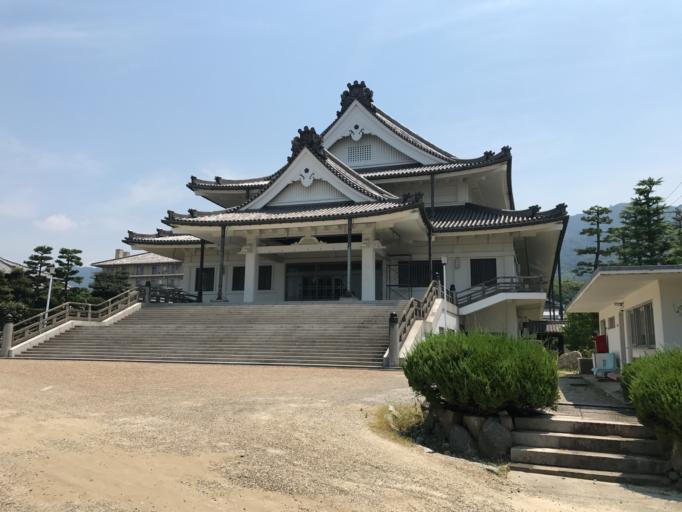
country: JP
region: Osaka
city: Yao
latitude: 34.6189
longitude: 135.6340
